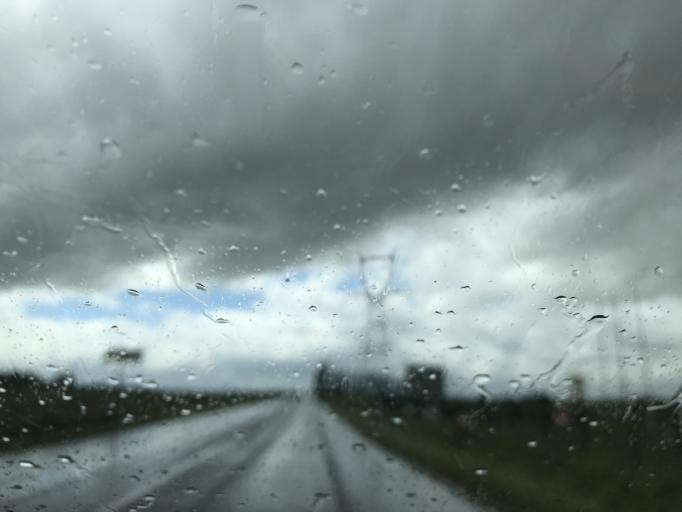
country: FR
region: Haute-Normandie
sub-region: Departement de l'Eure
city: Damville
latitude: 48.8747
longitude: 1.0977
